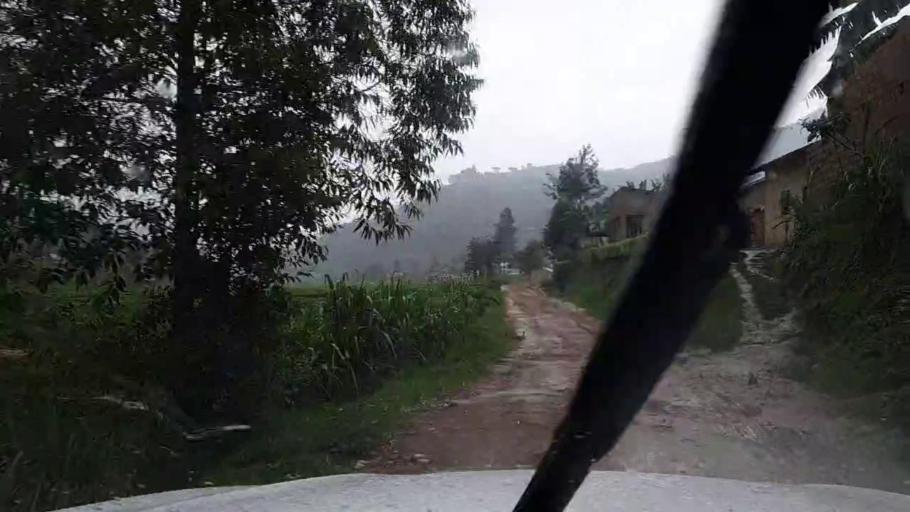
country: RW
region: Northern Province
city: Byumba
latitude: -1.6523
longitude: 29.9221
